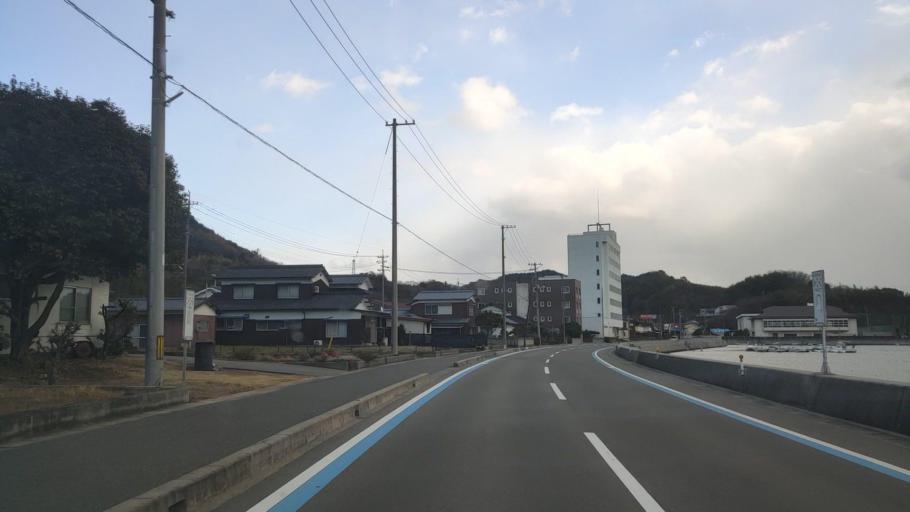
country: JP
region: Hiroshima
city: Innoshima
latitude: 34.2046
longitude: 133.0983
